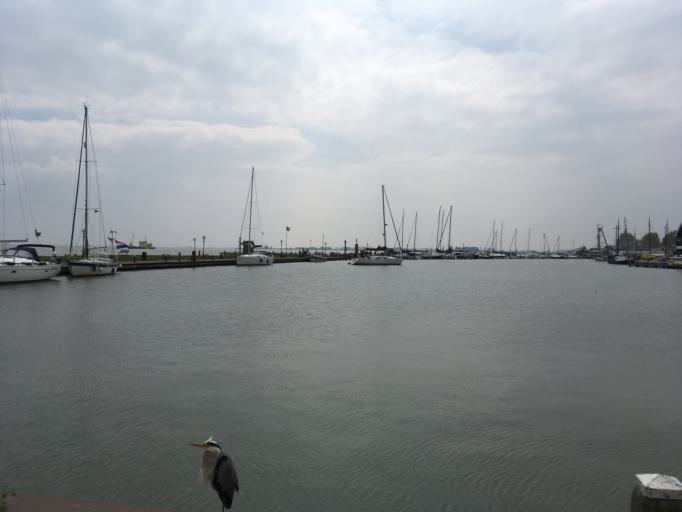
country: NL
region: North Holland
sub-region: Gemeente Edam-Volendam
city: Volendam
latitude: 52.4941
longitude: 5.0774
